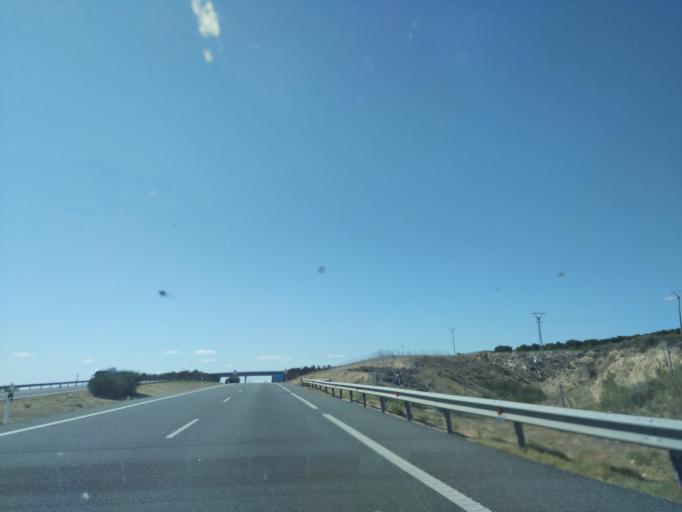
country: ES
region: Castille and Leon
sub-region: Provincia de Valladolid
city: Bercero
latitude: 41.5313
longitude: -5.0550
